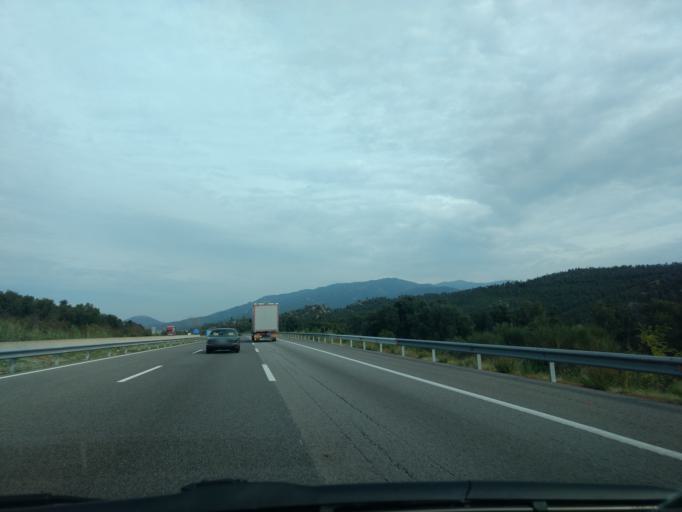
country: ES
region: Catalonia
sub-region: Provincia de Girona
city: Capmany
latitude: 42.3793
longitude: 2.8863
